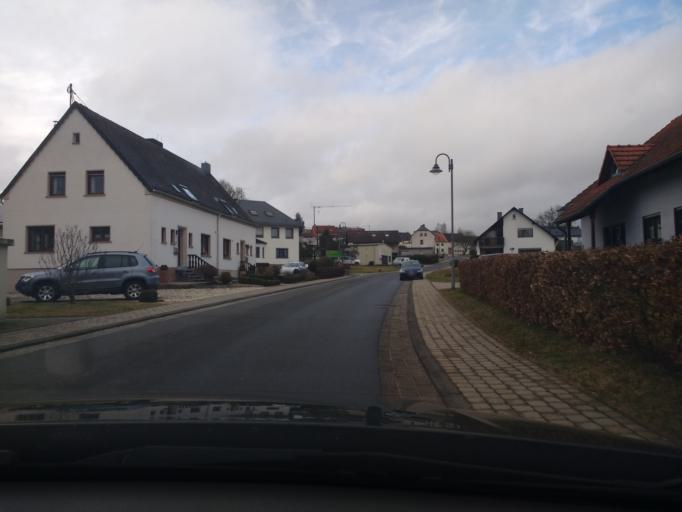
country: DE
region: Rheinland-Pfalz
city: Schillingen
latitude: 49.6320
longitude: 6.7856
